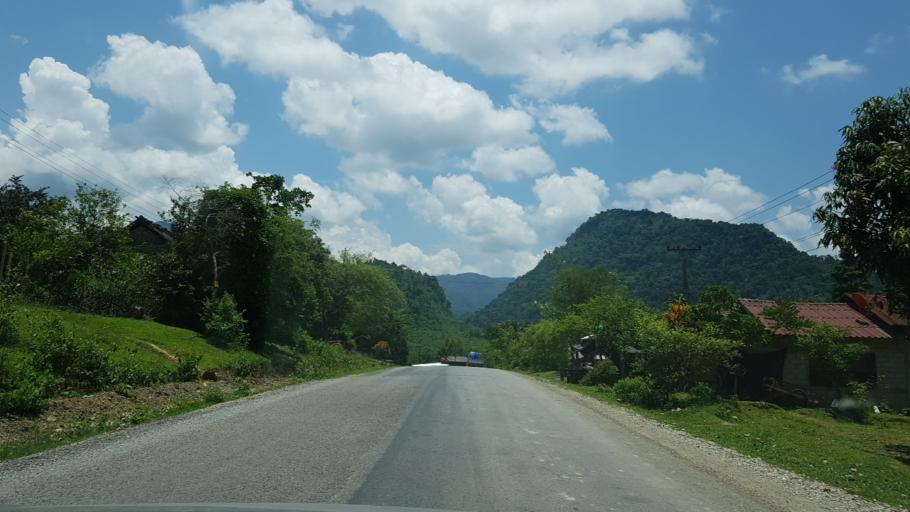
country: LA
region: Vientiane
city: Muang Kasi
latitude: 19.1338
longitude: 102.2206
